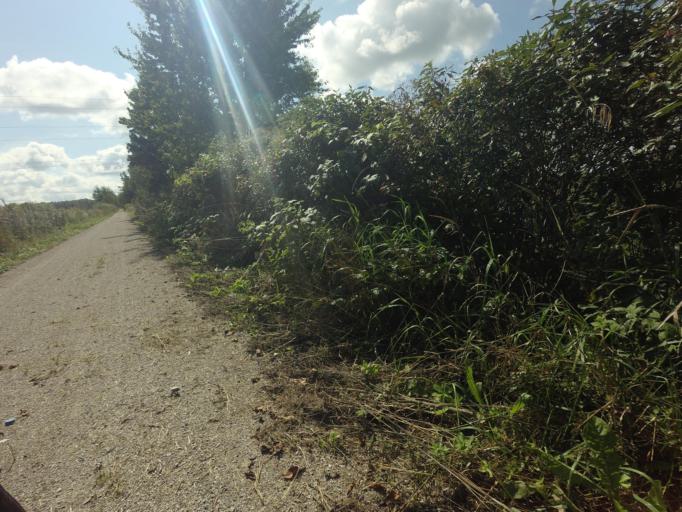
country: CA
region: Ontario
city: Huron East
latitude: 43.6969
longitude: -81.3401
